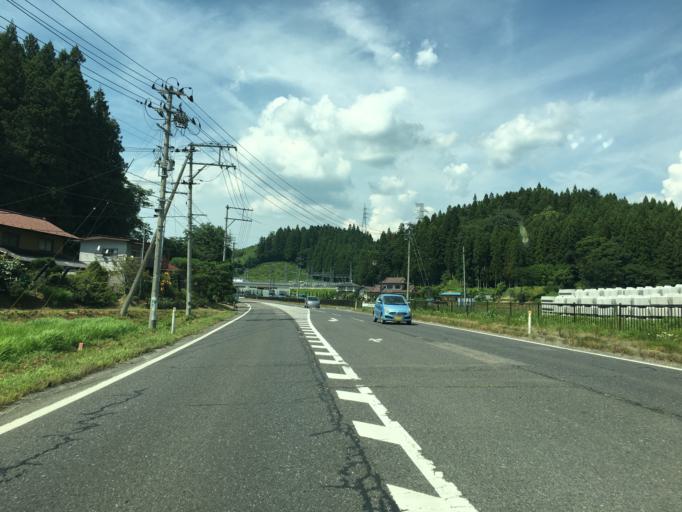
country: JP
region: Fukushima
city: Ishikawa
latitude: 37.2240
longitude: 140.5838
